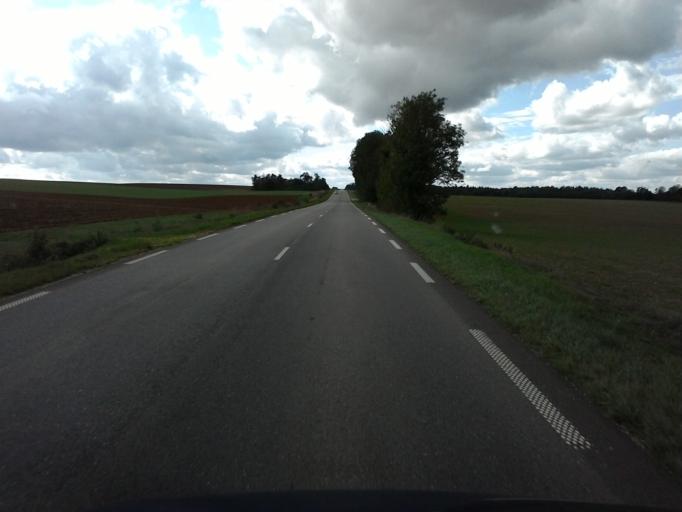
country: FR
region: Lorraine
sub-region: Departement des Vosges
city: Neufchateau
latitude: 48.4330
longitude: 5.7757
